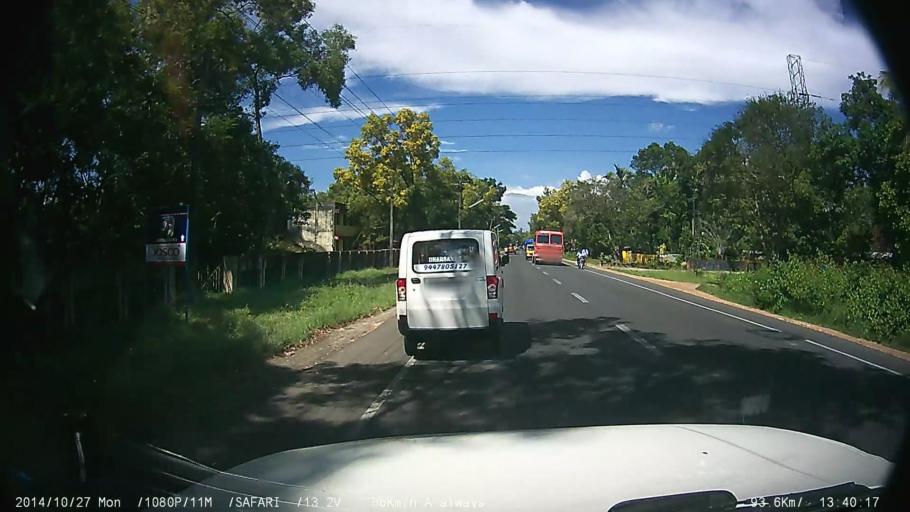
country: IN
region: Kerala
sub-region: Alappuzha
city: Shertallai
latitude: 9.6333
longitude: 76.3339
